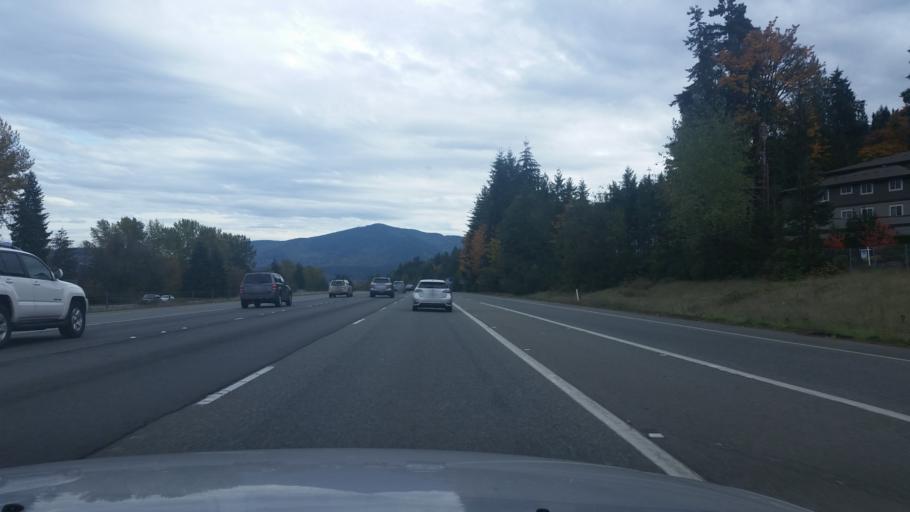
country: US
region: Washington
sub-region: King County
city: West Lake Sammamish
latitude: 47.5612
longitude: -122.0926
